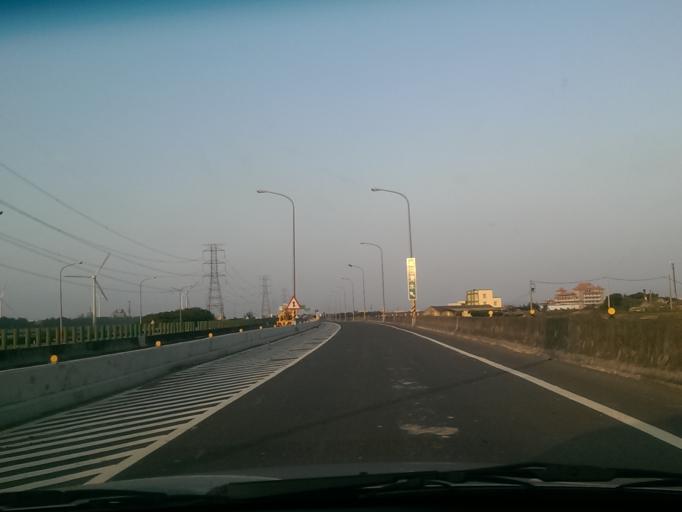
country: TW
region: Taiwan
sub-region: Changhua
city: Chang-hua
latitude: 24.1436
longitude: 120.4483
